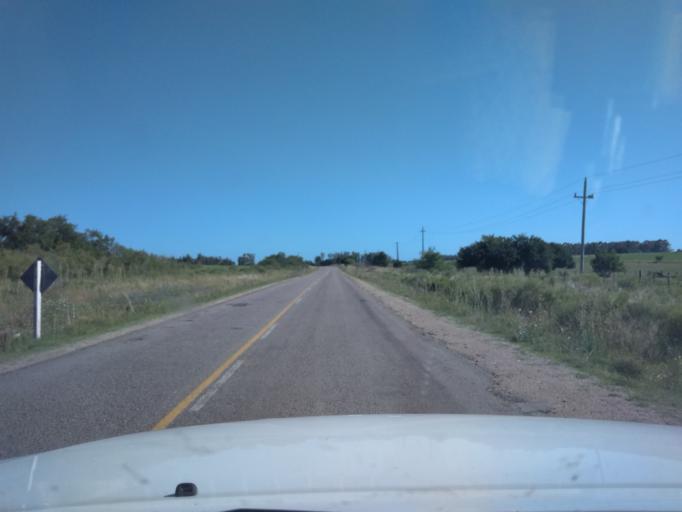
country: UY
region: Canelones
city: San Ramon
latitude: -34.2628
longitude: -55.9276
